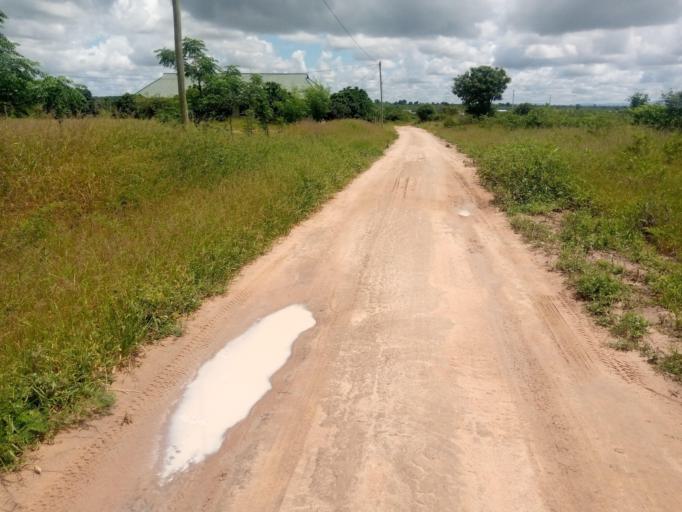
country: TZ
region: Dodoma
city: Dodoma
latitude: -6.1135
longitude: 35.7393
